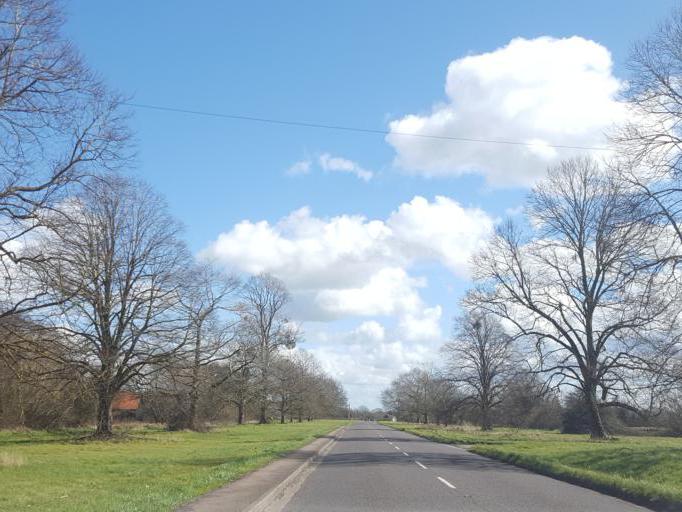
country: GB
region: England
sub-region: Worcestershire
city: Great Malvern
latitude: 52.1064
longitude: -2.2910
